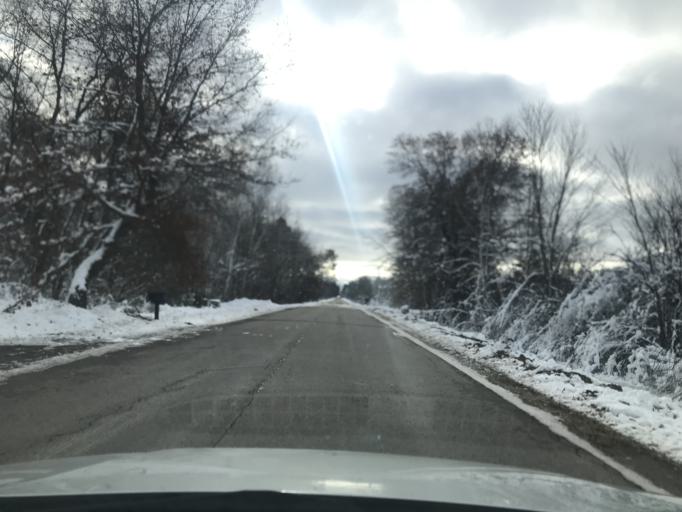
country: US
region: Wisconsin
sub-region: Marinette County
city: Peshtigo
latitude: 45.0773
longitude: -87.7216
